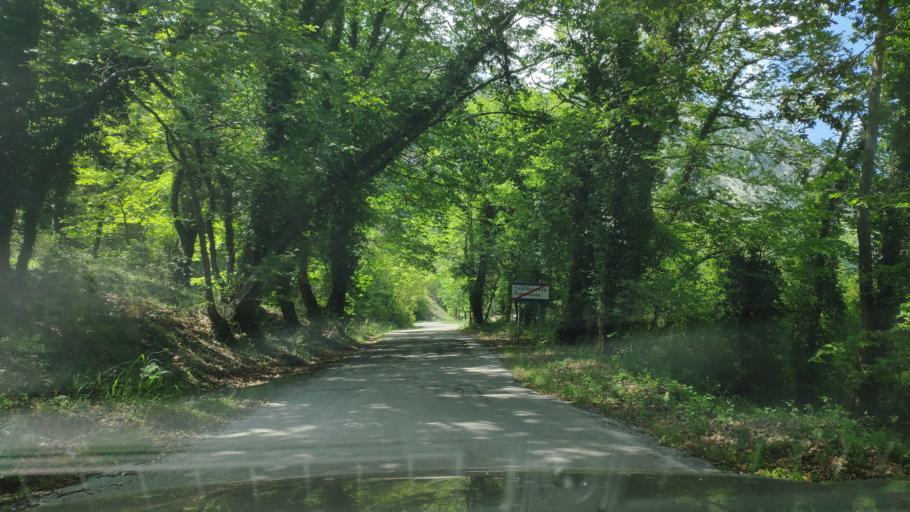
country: GR
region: Epirus
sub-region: Nomos Artas
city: Agios Dimitrios
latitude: 39.4358
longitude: 21.0149
